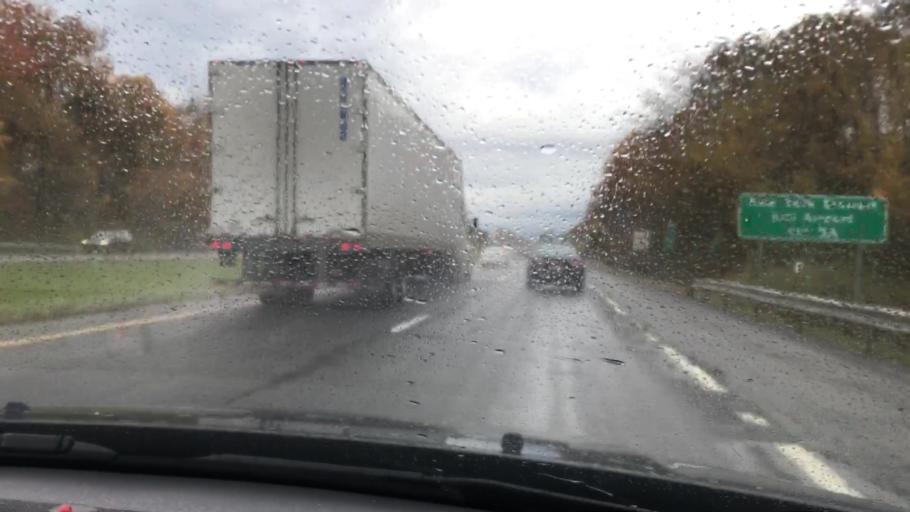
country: US
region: New York
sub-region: Orange County
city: Gardnertown
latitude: 41.5140
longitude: -74.0576
